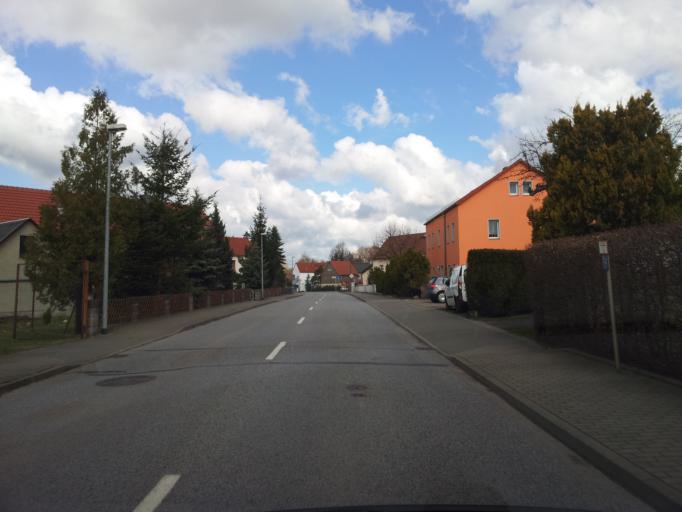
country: DE
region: Saxony
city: Ottendorf-Okrilla
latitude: 51.1820
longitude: 13.8470
